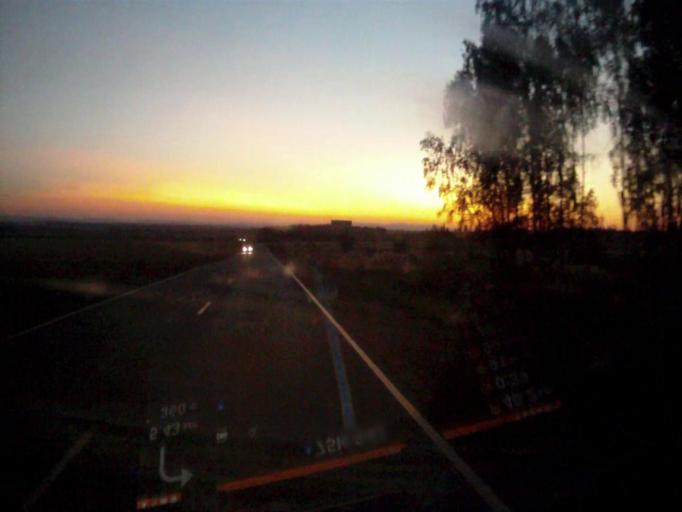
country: RU
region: Chelyabinsk
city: Timiryazevskiy
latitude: 55.2092
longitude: 60.6793
